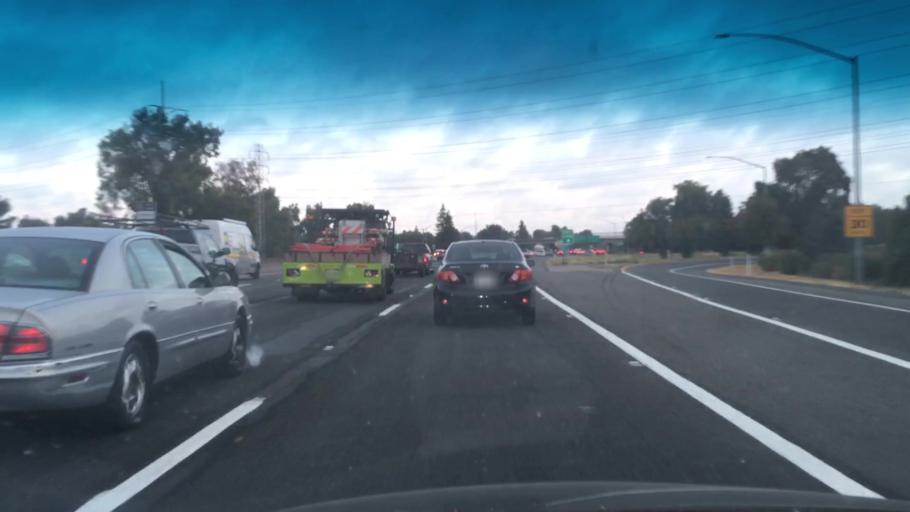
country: US
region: California
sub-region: Sacramento County
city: Parkway
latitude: 38.5074
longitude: -121.4577
